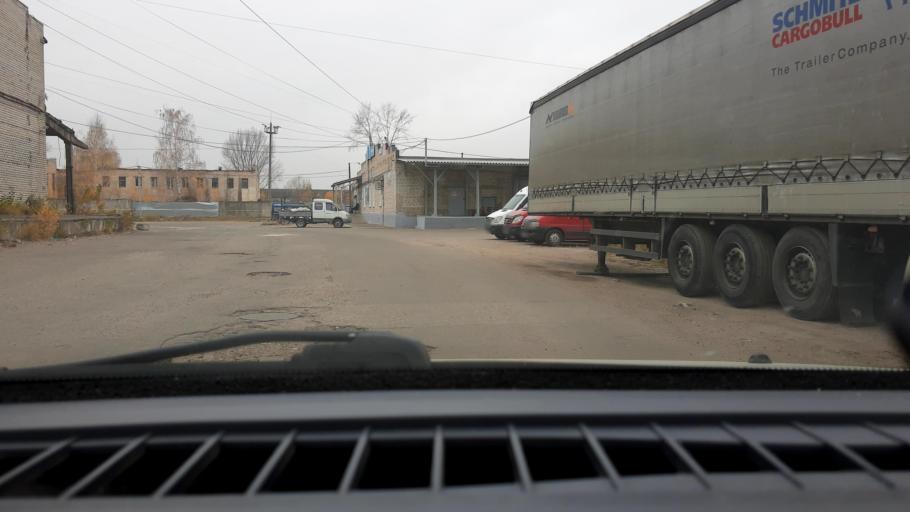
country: RU
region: Nizjnij Novgorod
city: Gorbatovka
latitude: 56.3370
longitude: 43.8127
